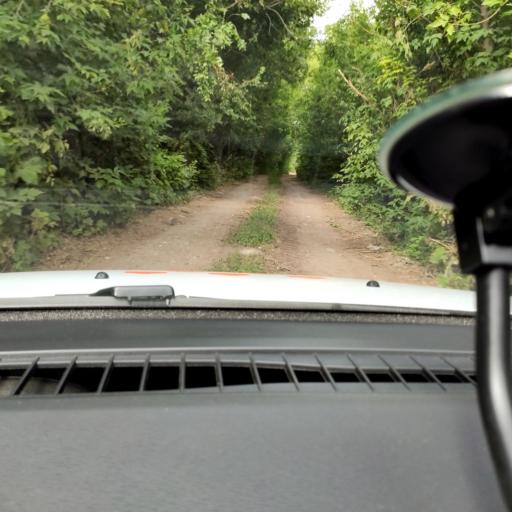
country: RU
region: Samara
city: Samara
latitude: 53.1791
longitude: 50.2173
